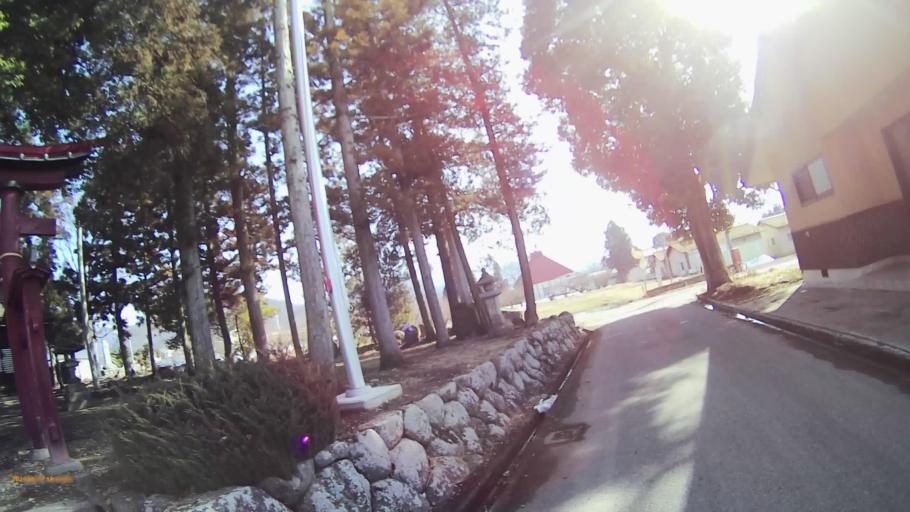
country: JP
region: Nagano
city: Nakano
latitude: 36.7567
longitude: 138.3733
